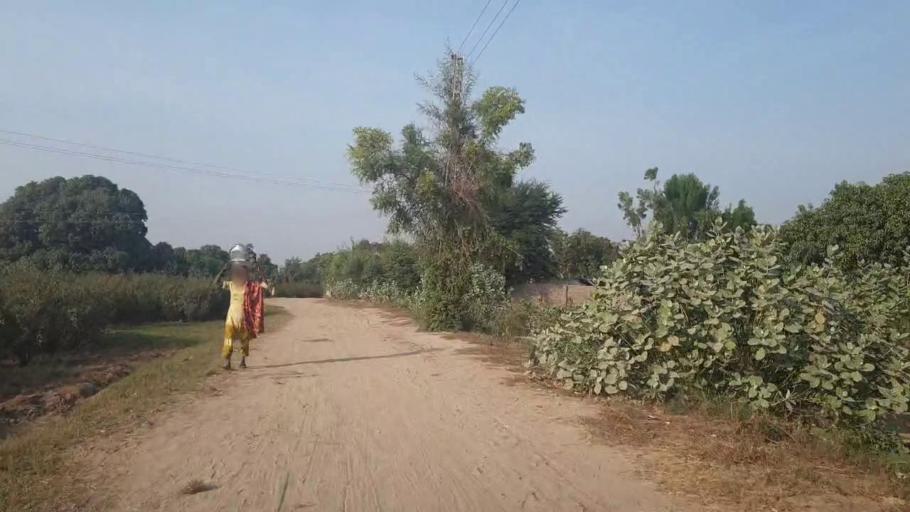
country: PK
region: Sindh
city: Tando Jam
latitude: 25.4276
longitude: 68.4649
